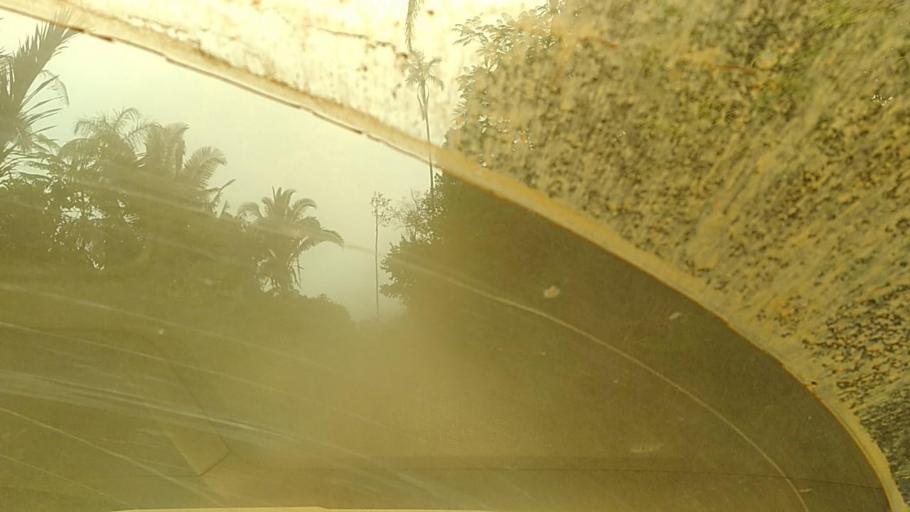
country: BR
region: Rondonia
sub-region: Porto Velho
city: Porto Velho
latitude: -8.7729
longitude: -63.1954
